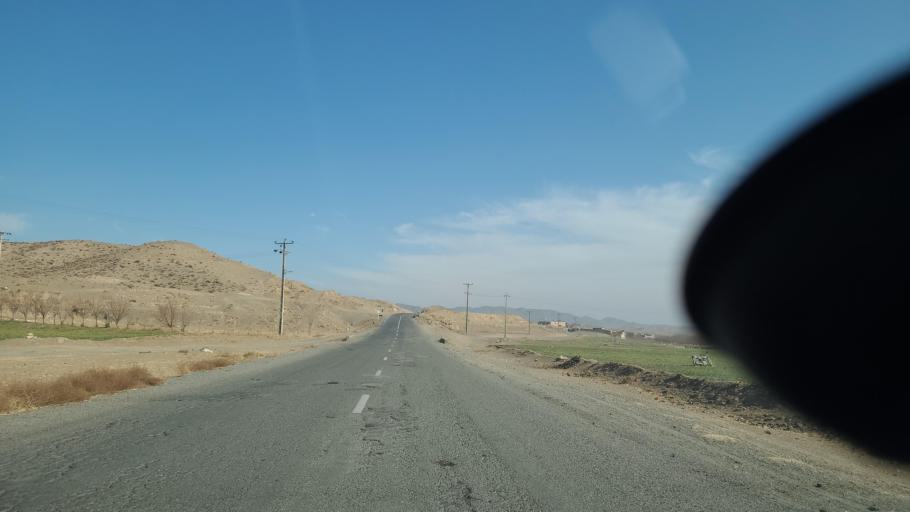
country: IR
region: Razavi Khorasan
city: Fariman
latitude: 35.5905
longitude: 59.6711
